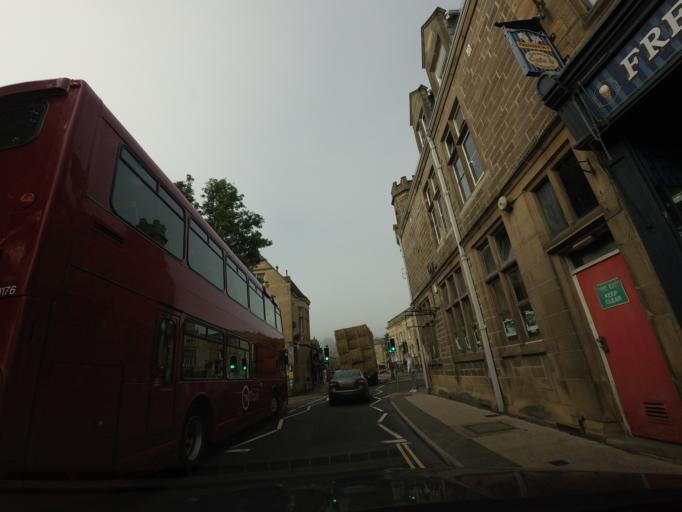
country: GB
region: England
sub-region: Derbyshire
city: Bakewell
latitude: 53.2136
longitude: -1.6745
